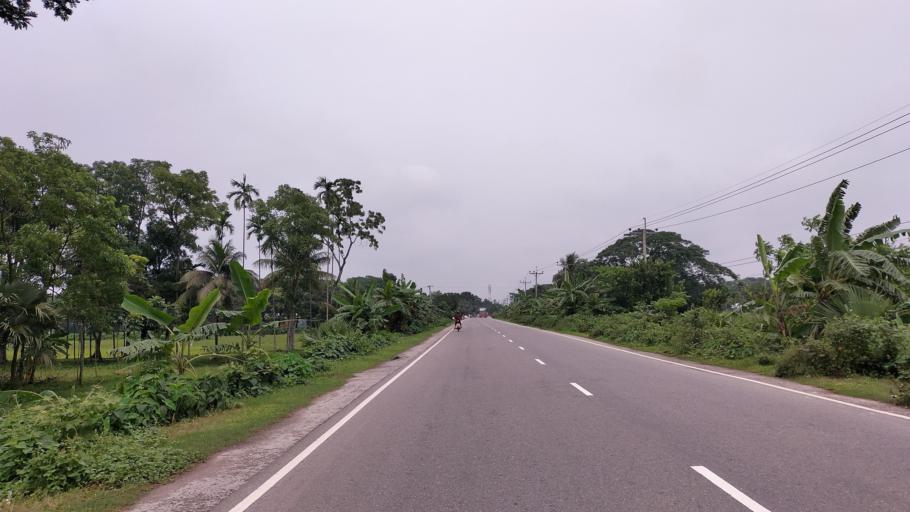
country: BD
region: Dhaka
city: Netrakona
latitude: 24.8506
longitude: 90.6342
